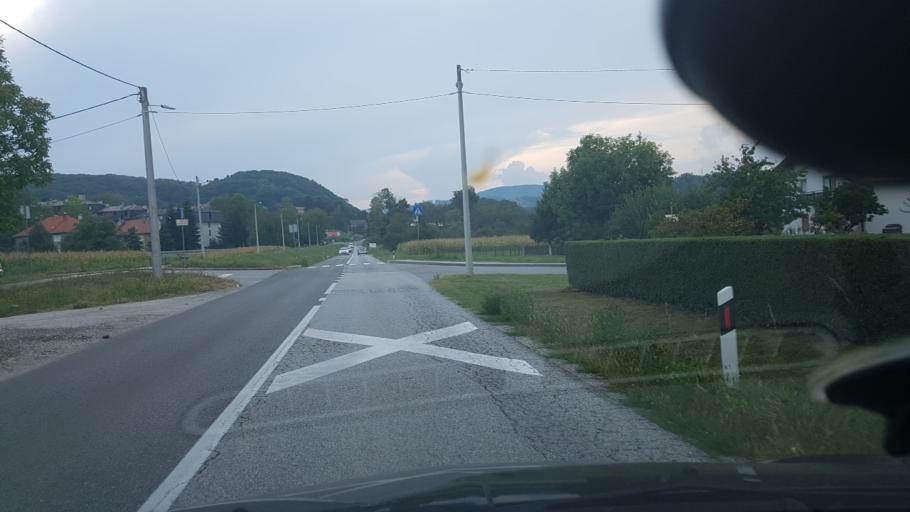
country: HR
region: Zagrebacka
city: Bregana
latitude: 45.8399
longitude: 15.6927
